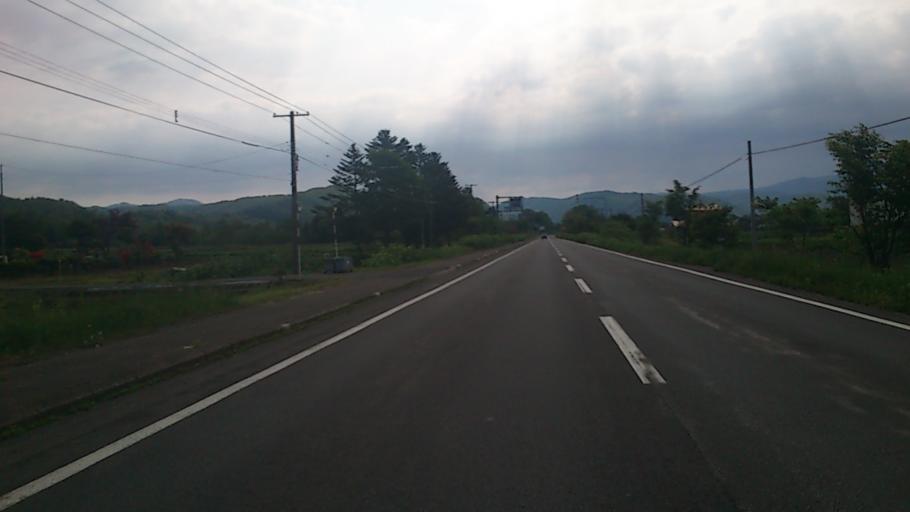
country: JP
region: Hokkaido
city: Kamikawa
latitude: 43.8492
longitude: 142.7397
